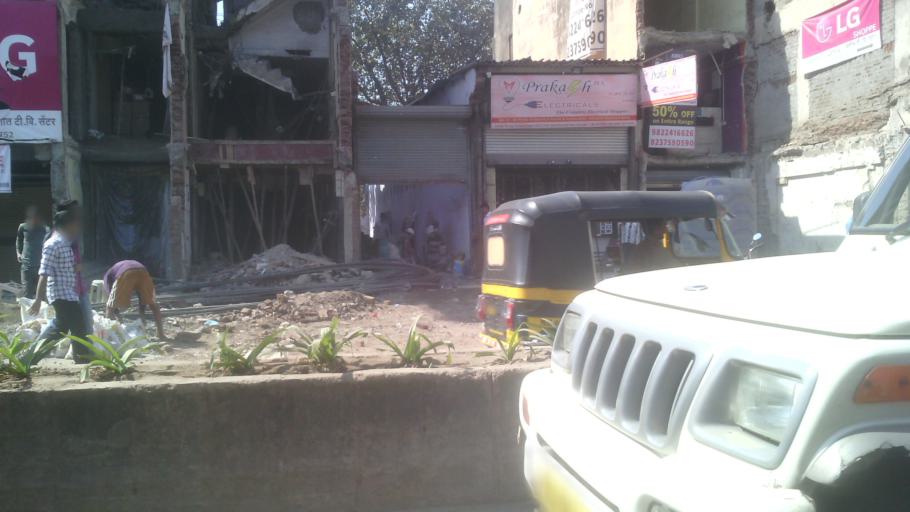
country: IN
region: Maharashtra
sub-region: Thane
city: Ulhasnagar
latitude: 19.2244
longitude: 73.1626
